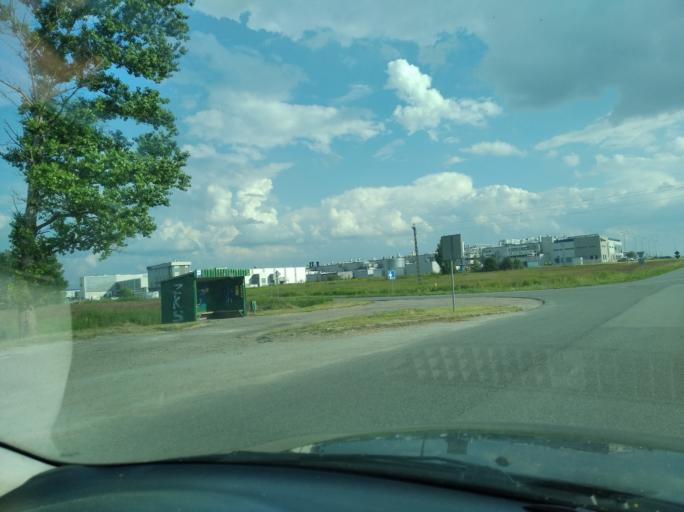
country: PL
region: Subcarpathian Voivodeship
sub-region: Powiat rzeszowski
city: Wysoka Glogowska
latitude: 50.1251
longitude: 22.0250
